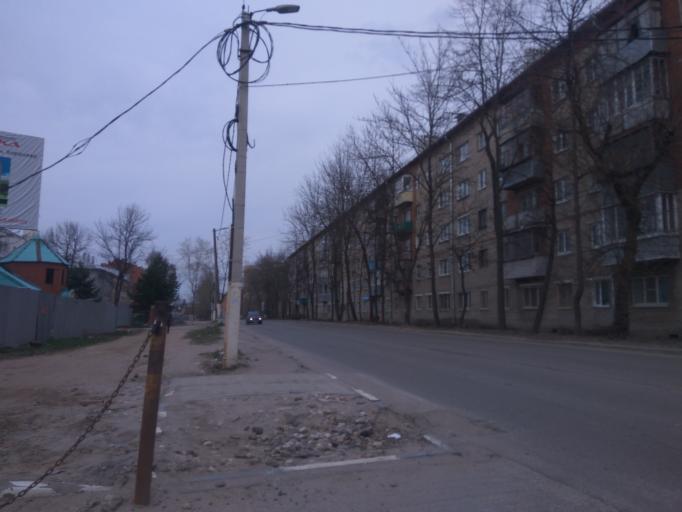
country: RU
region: Vladimir
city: Aleksandrov
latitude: 56.3990
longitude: 38.7077
